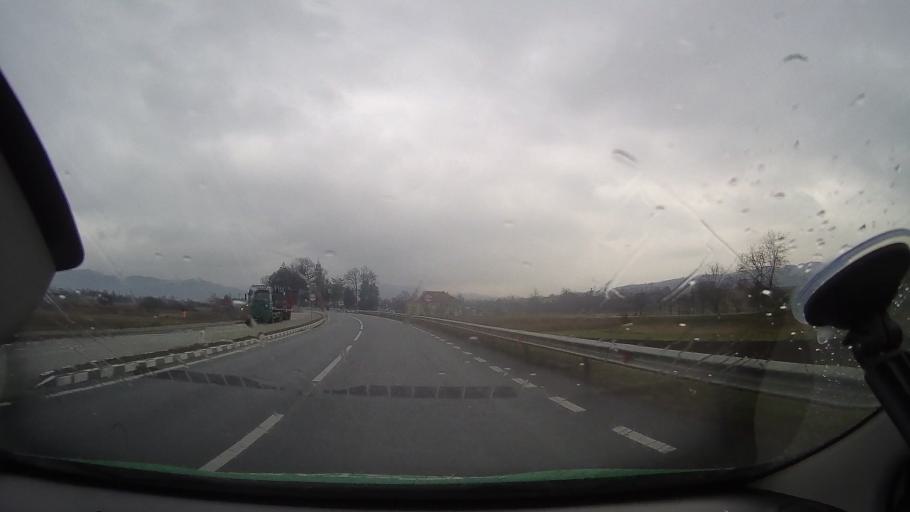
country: RO
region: Hunedoara
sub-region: Comuna Baia de Cris
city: Baia de Cris
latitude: 46.1688
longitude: 22.7315
